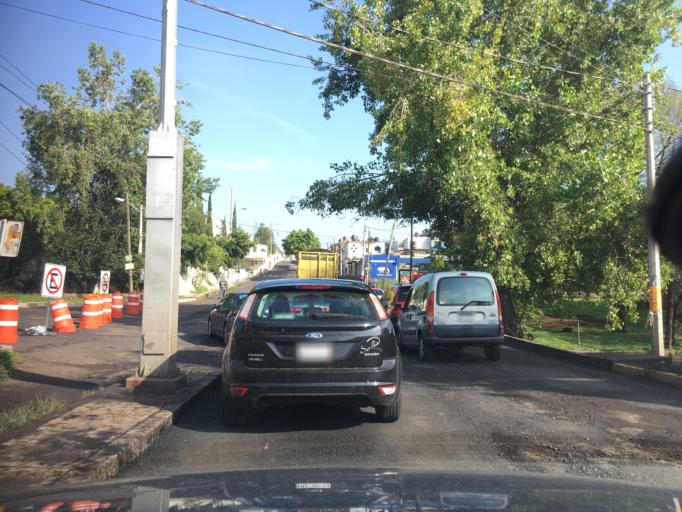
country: MX
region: Michoacan
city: Morelia
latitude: 19.7205
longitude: -101.1790
